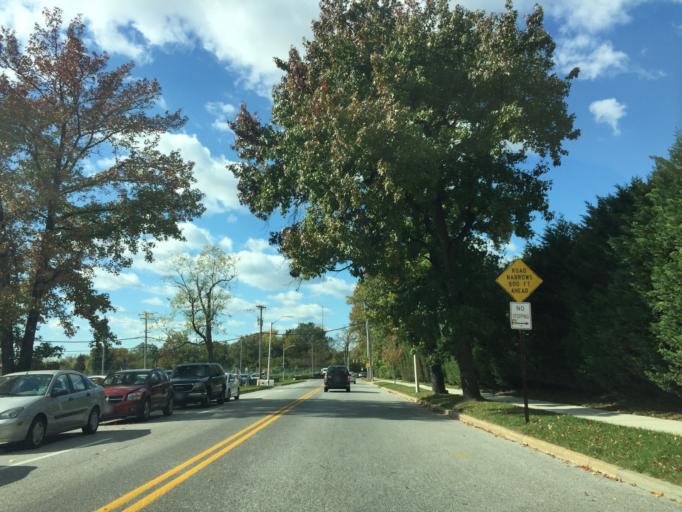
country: US
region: Maryland
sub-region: City of Baltimore
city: Baltimore
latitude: 39.3458
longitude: -76.6146
